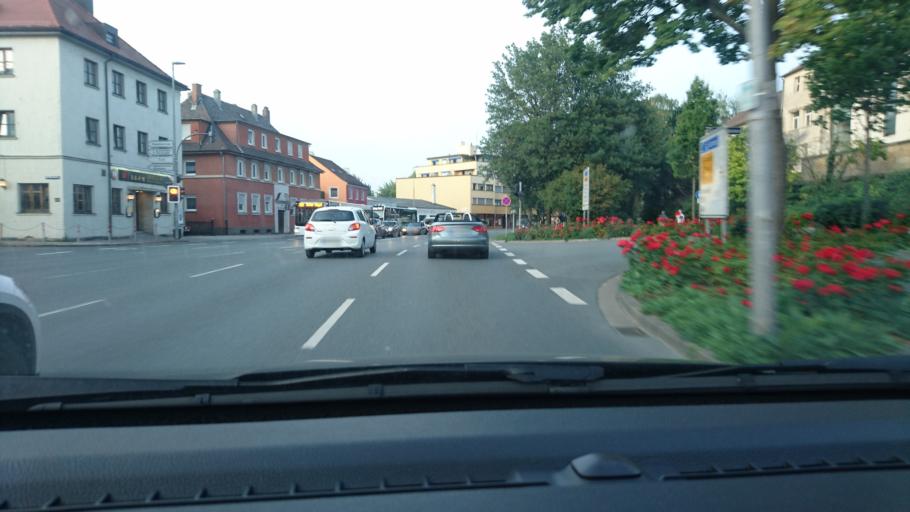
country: DE
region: Bavaria
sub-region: Upper Franconia
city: Bayreuth
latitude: 49.9454
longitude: 11.5714
